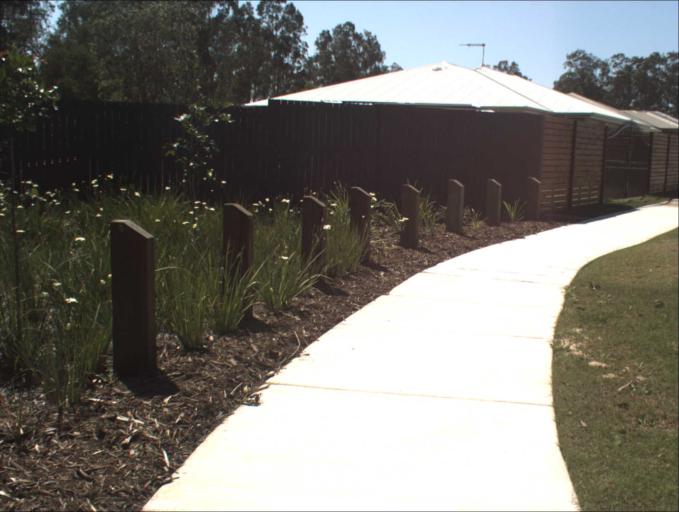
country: AU
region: Queensland
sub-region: Logan
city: Waterford West
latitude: -27.7119
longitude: 153.1427
